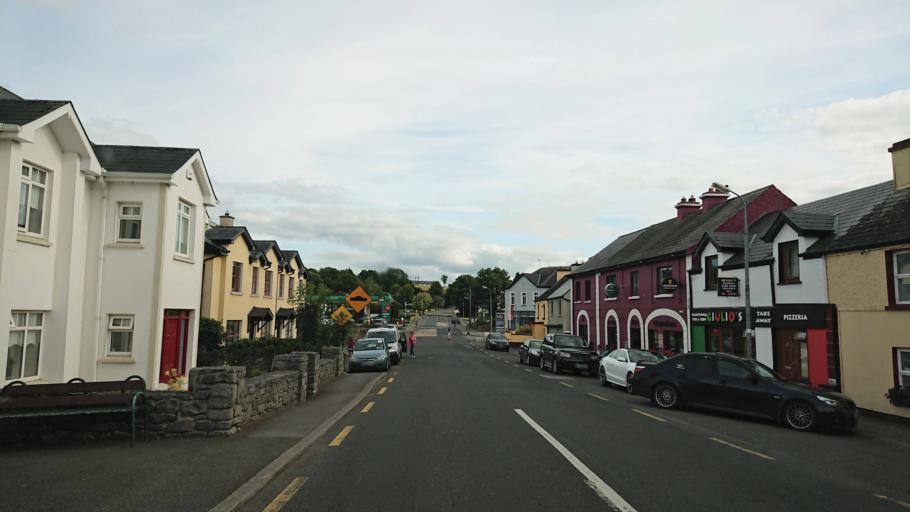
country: IE
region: Connaught
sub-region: County Leitrim
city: Carrick-on-Shannon
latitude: 53.9901
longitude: -8.0649
